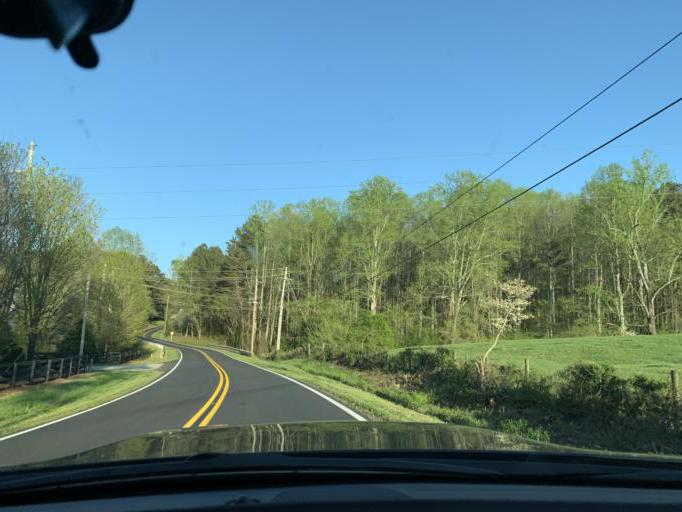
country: US
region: Georgia
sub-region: Forsyth County
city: Cumming
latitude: 34.2581
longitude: -84.2089
